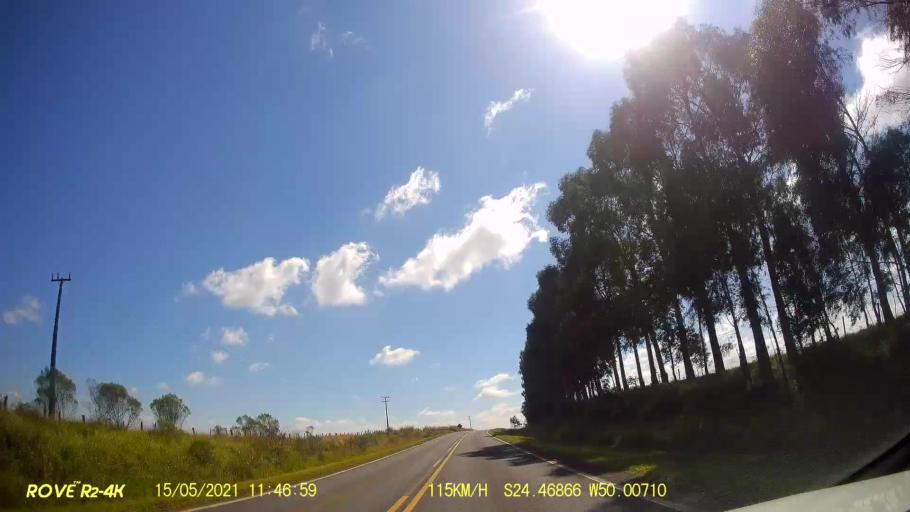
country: BR
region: Parana
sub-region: Pirai Do Sul
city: Pirai do Sul
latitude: -24.4688
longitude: -50.0071
